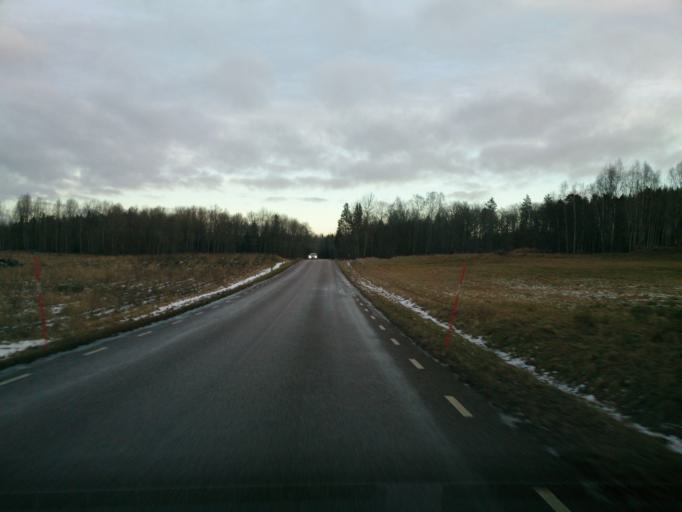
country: SE
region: OEstergoetland
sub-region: Atvidabergs Kommun
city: Atvidaberg
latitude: 58.2777
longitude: 16.0337
